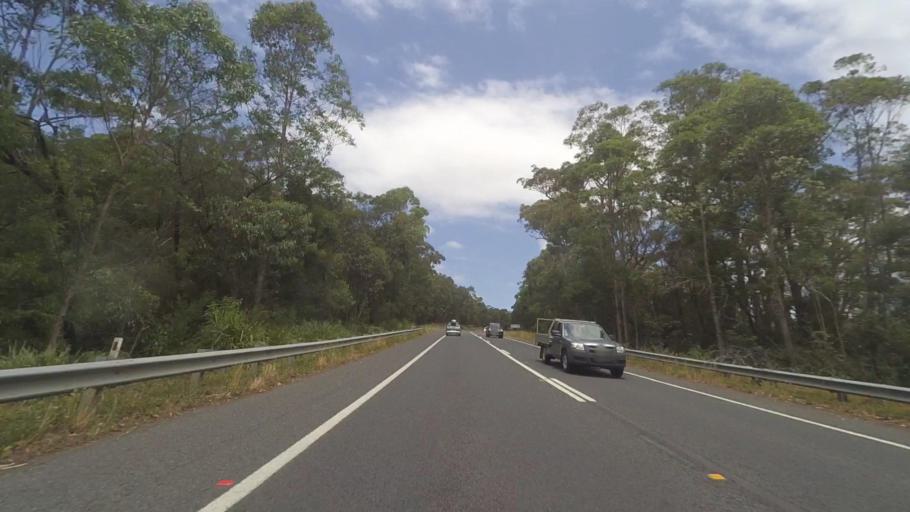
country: AU
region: New South Wales
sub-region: Shoalhaven Shire
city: Milton
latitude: -35.2280
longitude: 150.4352
